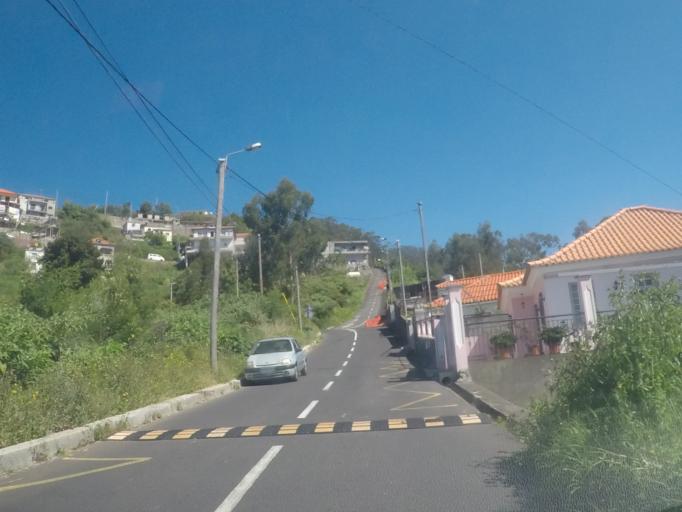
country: PT
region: Madeira
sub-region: Camara de Lobos
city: Curral das Freiras
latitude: 32.6817
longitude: -16.9679
